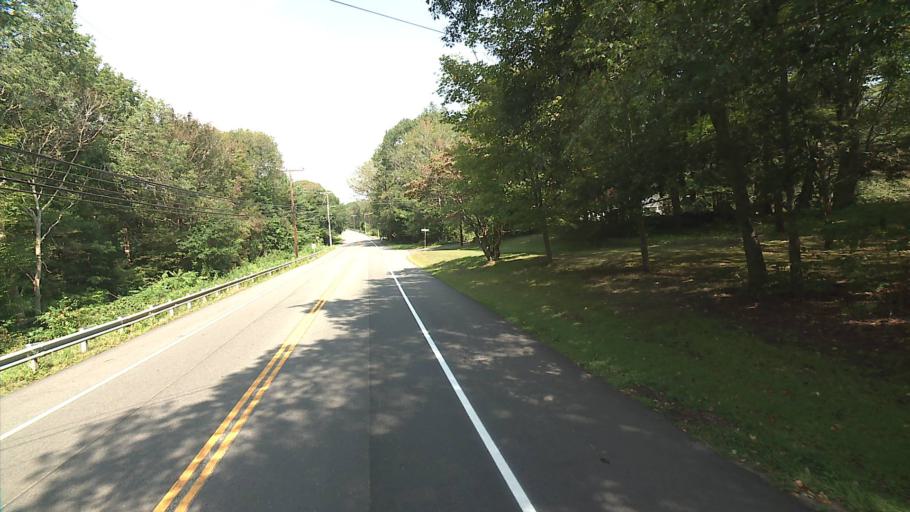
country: US
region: Connecticut
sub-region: New Haven County
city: Madison Center
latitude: 41.3469
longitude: -72.6314
